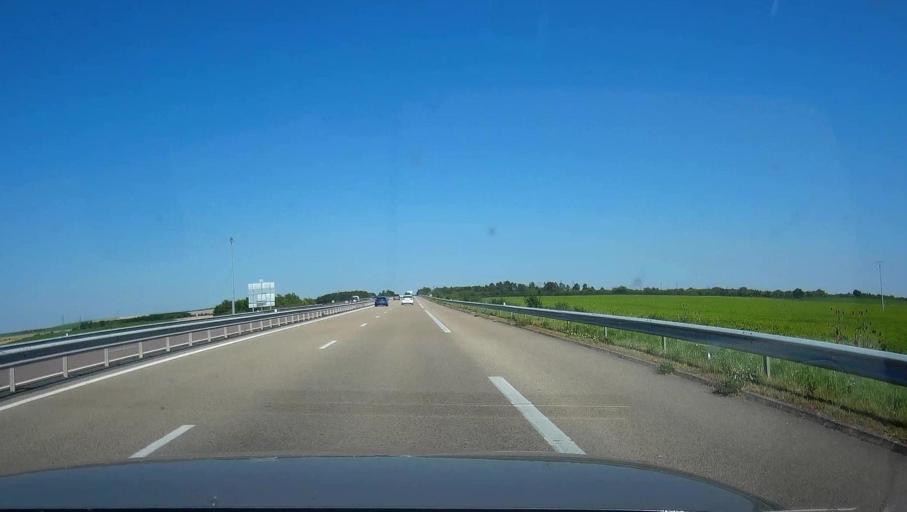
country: FR
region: Champagne-Ardenne
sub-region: Departement de l'Aube
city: Creney-pres-Troyes
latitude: 48.3396
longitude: 4.1665
